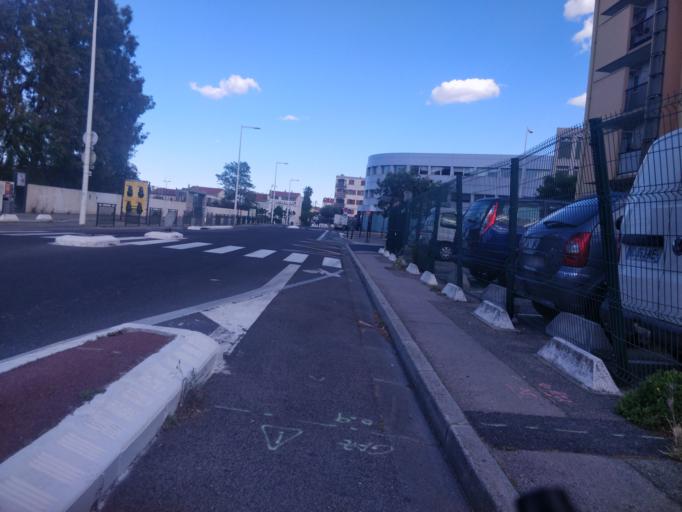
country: FR
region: Languedoc-Roussillon
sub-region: Departement des Pyrenees-Orientales
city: Perpignan
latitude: 42.6909
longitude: 2.9083
